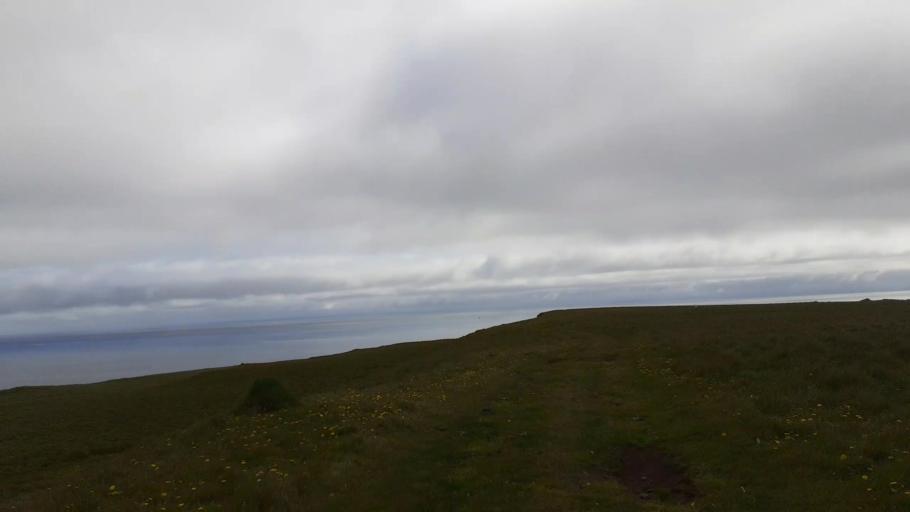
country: IS
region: Northeast
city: Dalvik
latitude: 66.5404
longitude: -17.9840
